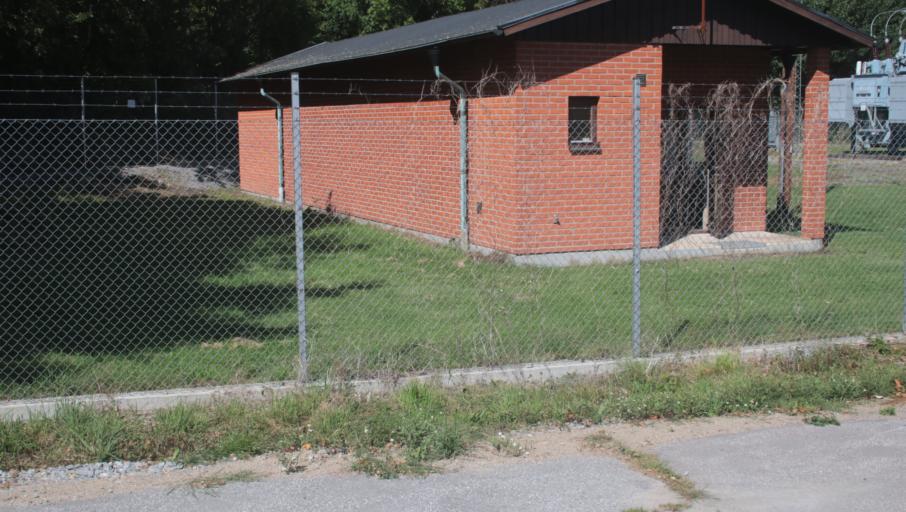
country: SE
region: Blekinge
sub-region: Karlshamns Kommun
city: Morrum
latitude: 56.1954
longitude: 14.7649
